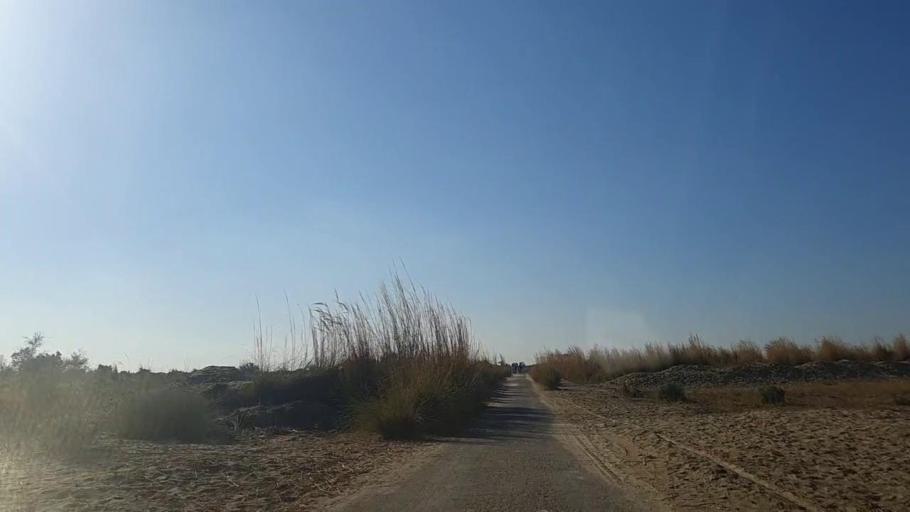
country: PK
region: Sindh
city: Sanghar
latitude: 26.2419
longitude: 68.8964
